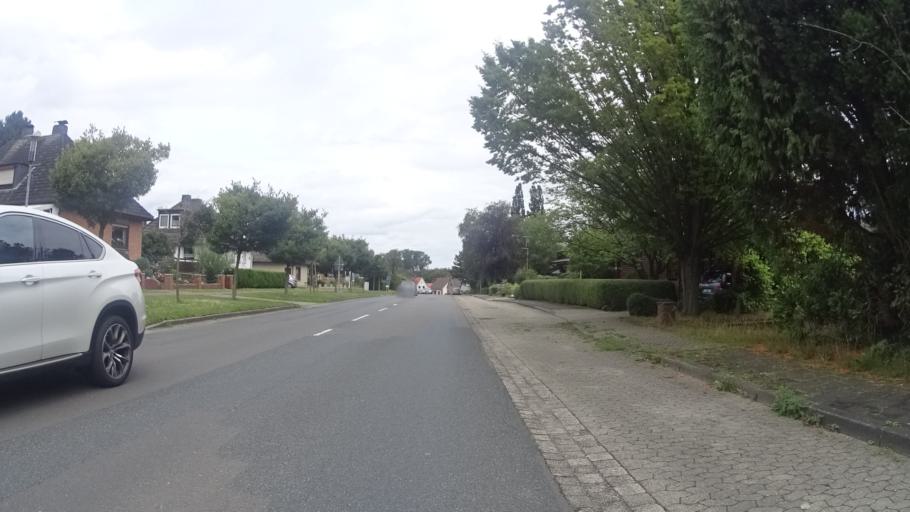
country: DE
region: Lower Saxony
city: Lintig
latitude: 53.6172
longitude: 8.8464
